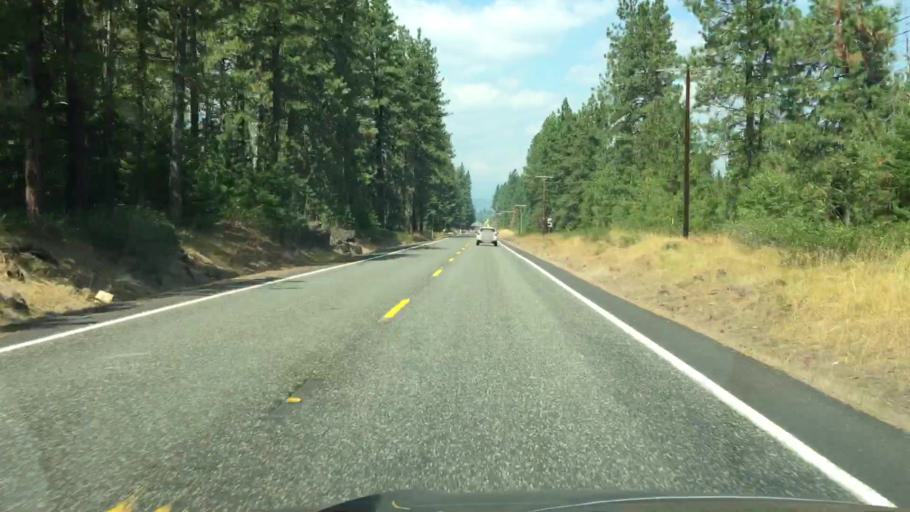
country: US
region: Washington
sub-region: Klickitat County
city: White Salmon
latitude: 45.9813
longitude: -121.5084
